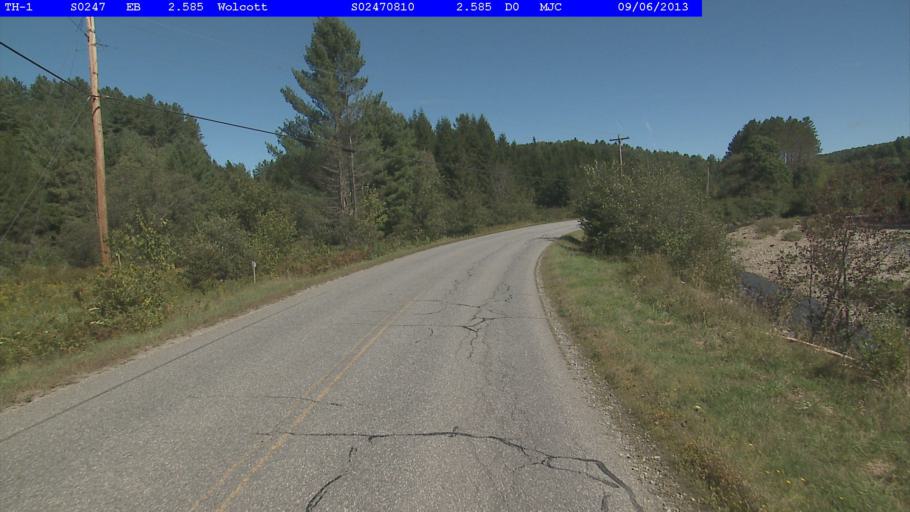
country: US
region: Vermont
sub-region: Lamoille County
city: Morrisville
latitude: 44.5927
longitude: -72.4741
